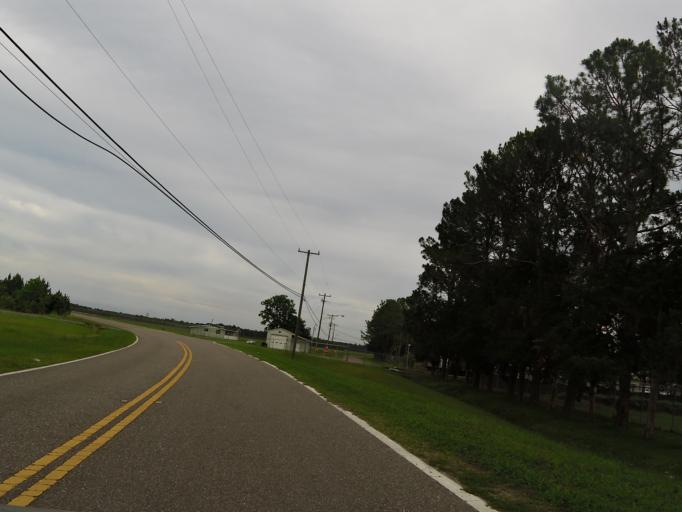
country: US
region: Florida
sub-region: Nassau County
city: Nassau Village-Ratliff
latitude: 30.5469
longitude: -81.7287
